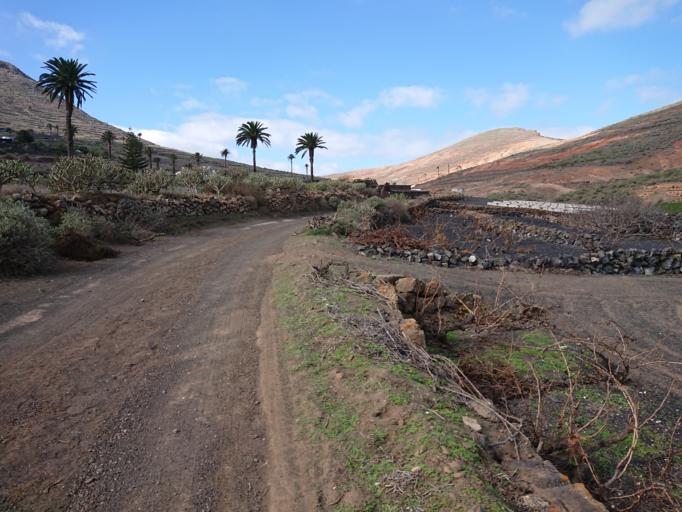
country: ES
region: Canary Islands
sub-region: Provincia de Las Palmas
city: Haria
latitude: 29.1438
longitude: -13.5084
